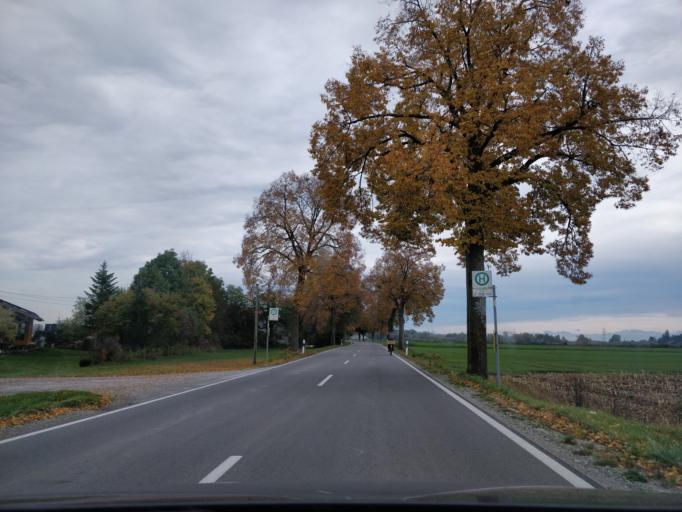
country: DE
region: Bavaria
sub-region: Swabia
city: Wiedergeltingen
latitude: 48.0328
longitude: 10.6887
